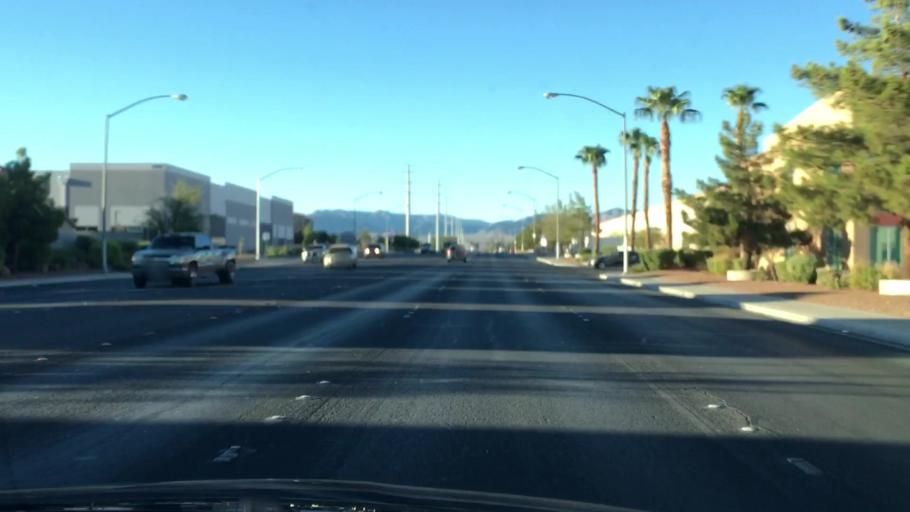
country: US
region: Nevada
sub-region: Clark County
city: Nellis Air Force Base
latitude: 36.2367
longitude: -115.0800
